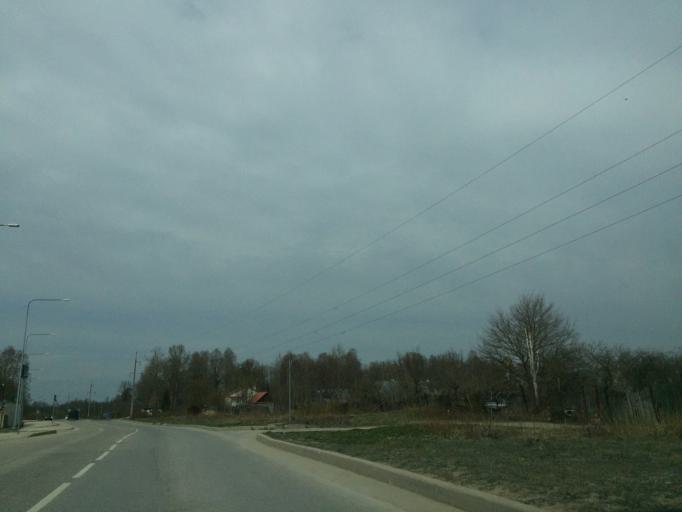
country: EE
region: Ida-Virumaa
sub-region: Narva linn
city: Narva
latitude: 59.3950
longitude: 28.1807
